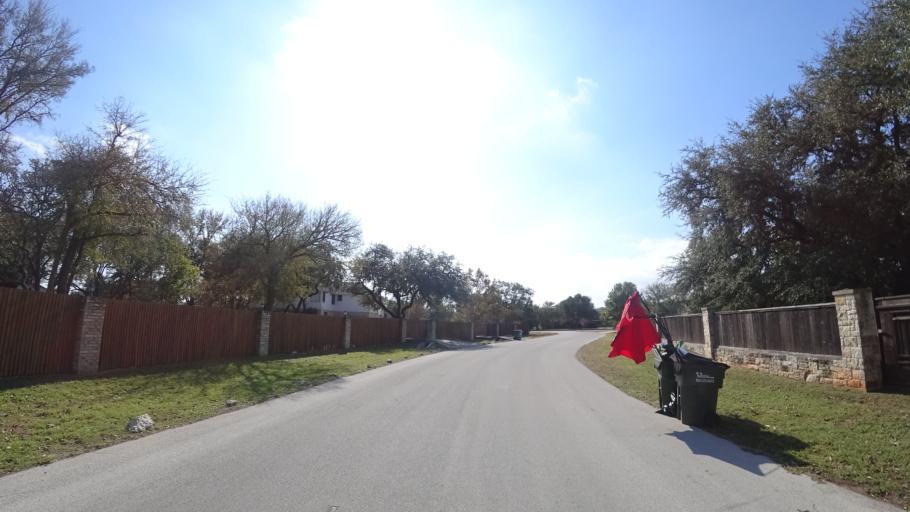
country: US
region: Texas
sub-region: Travis County
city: Shady Hollow
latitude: 30.1624
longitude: -97.8622
